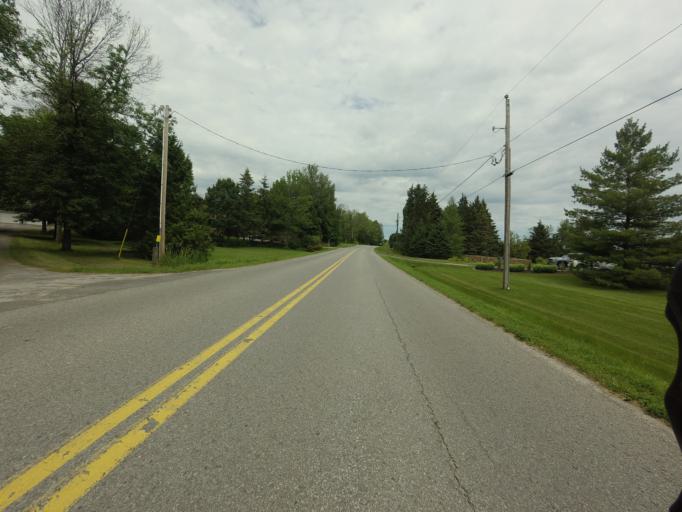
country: CA
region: Ontario
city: Bells Corners
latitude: 45.0575
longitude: -75.6109
